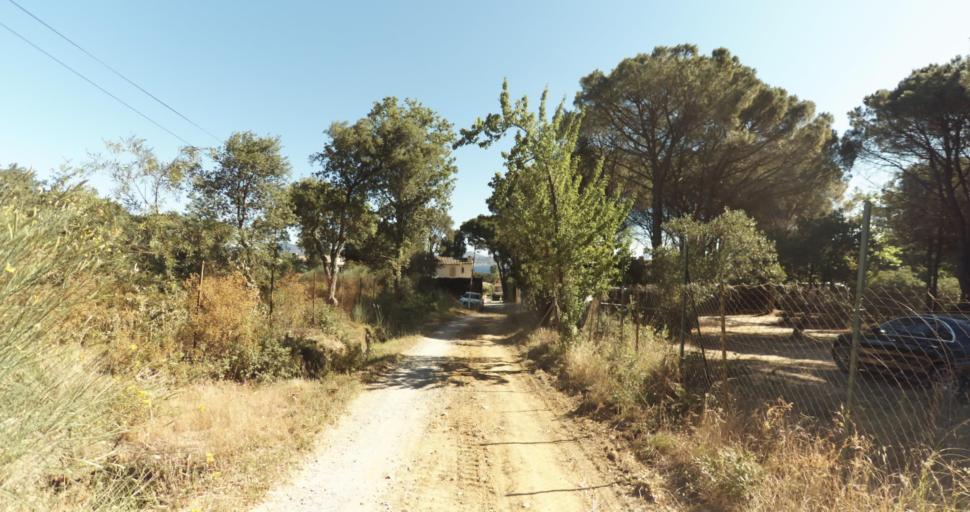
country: FR
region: Provence-Alpes-Cote d'Azur
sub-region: Departement du Var
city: Saint-Tropez
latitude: 43.2594
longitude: 6.6174
